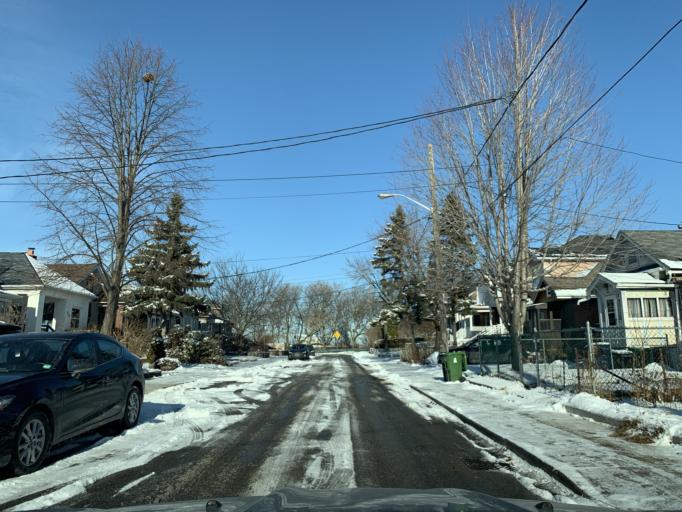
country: CA
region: Ontario
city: Toronto
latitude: 43.6712
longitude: -79.4848
